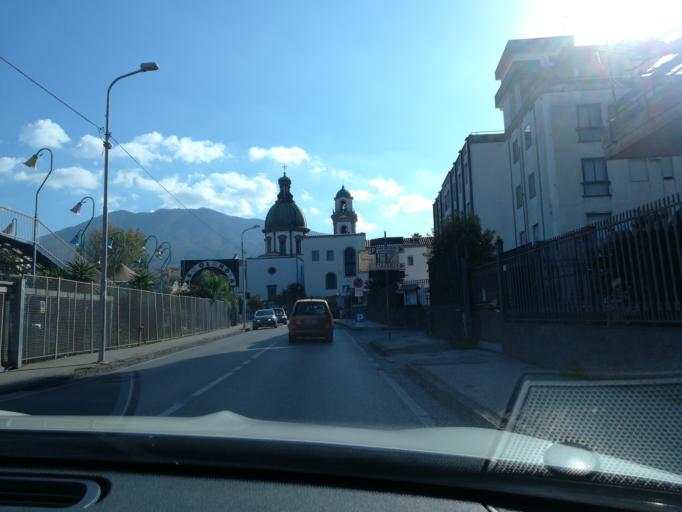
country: IT
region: Campania
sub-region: Provincia di Napoli
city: Sant'Anastasia
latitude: 40.8712
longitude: 14.3876
